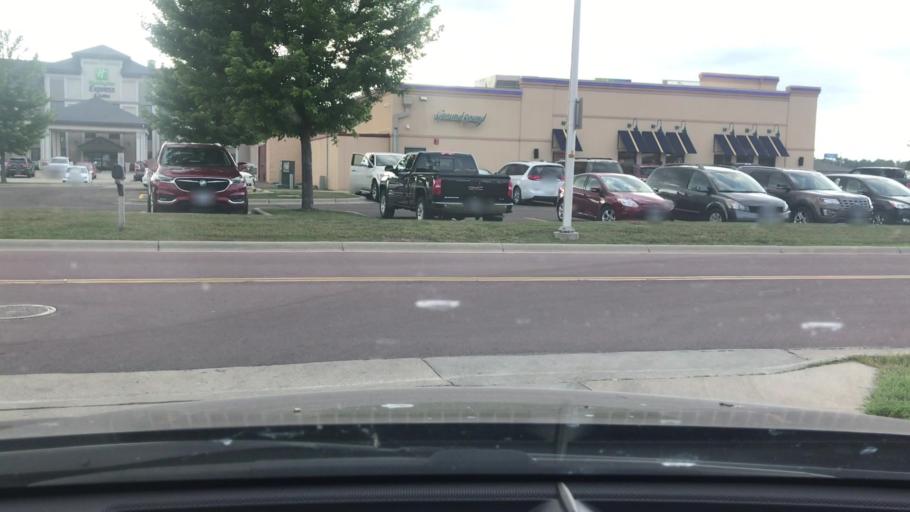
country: US
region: Minnesota
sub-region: Nobles County
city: Worthington
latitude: 43.6350
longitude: -95.5915
